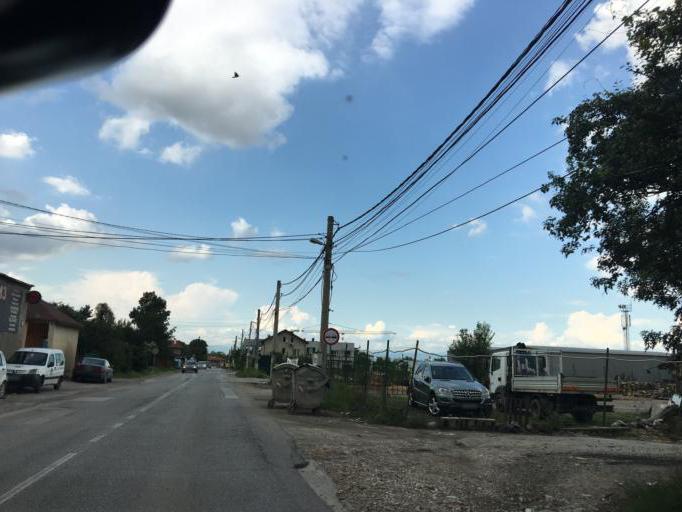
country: BG
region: Sofia-Capital
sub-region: Stolichna Obshtina
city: Sofia
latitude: 42.6367
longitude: 23.3535
